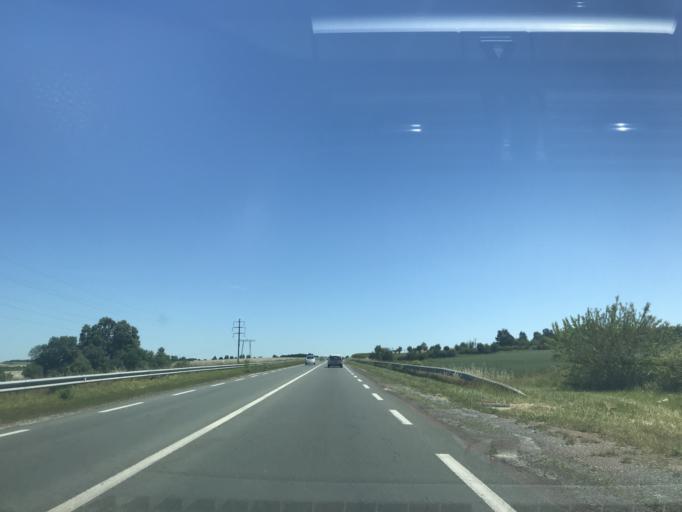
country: FR
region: Poitou-Charentes
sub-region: Departement de la Charente-Maritime
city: Saint-Georges-de-Didonne
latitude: 45.6142
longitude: -0.9849
